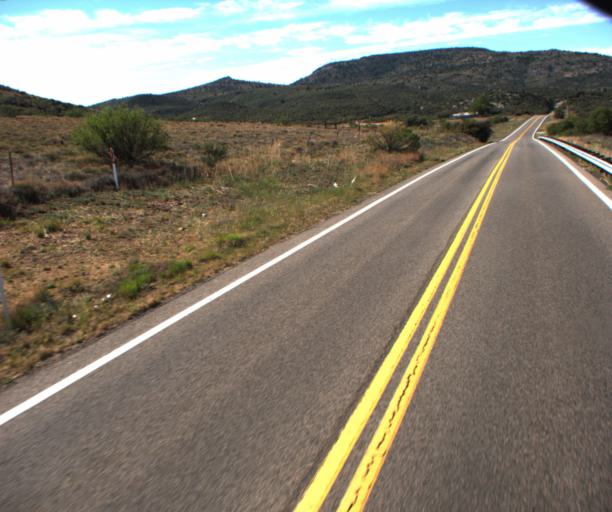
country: US
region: Arizona
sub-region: Yavapai County
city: Congress
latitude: 34.2443
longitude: -112.7366
